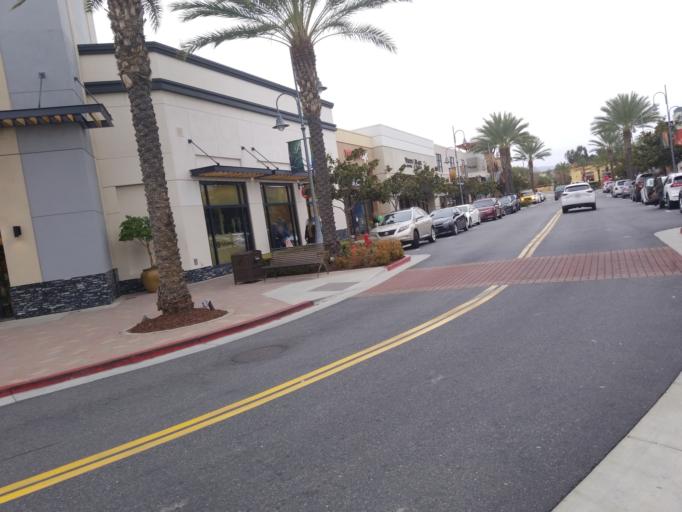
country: US
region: California
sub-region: Riverside County
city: Temecula
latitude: 33.5242
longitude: -117.1531
